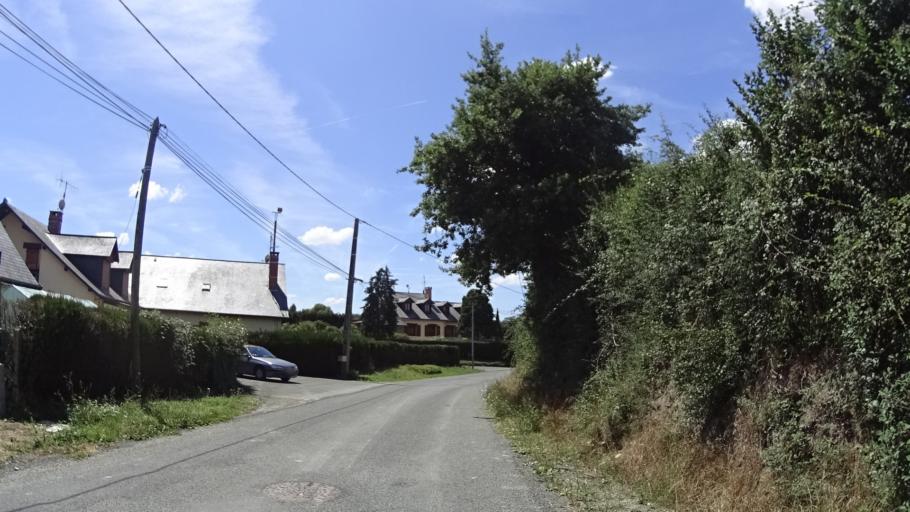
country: FR
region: Pays de la Loire
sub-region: Departement de Maine-et-Loire
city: Segre
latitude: 47.6197
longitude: -0.8874
